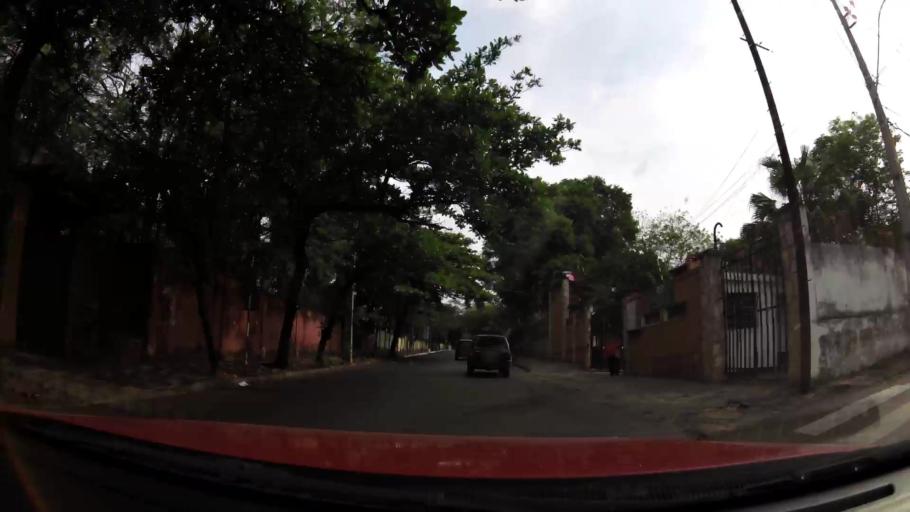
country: PY
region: Asuncion
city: Asuncion
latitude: -25.2900
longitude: -57.6101
